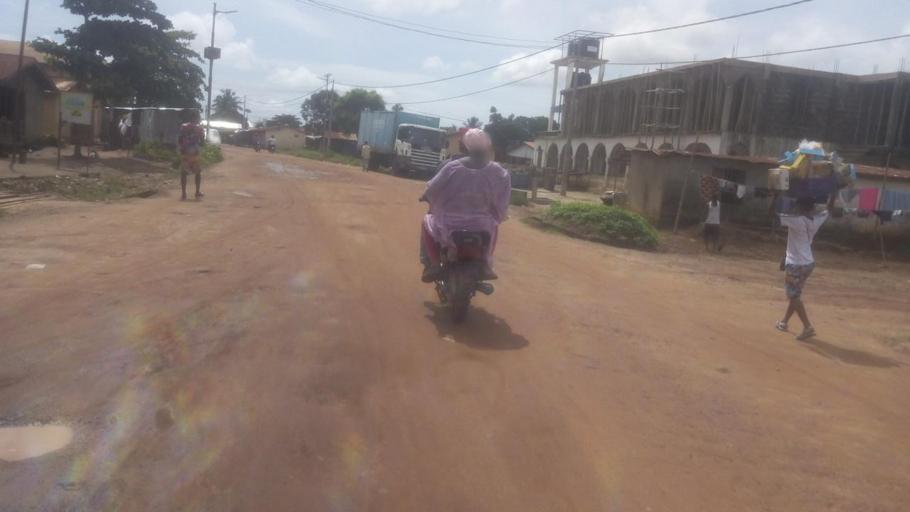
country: SL
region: Northern Province
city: Masoyila
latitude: 8.6019
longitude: -13.1831
